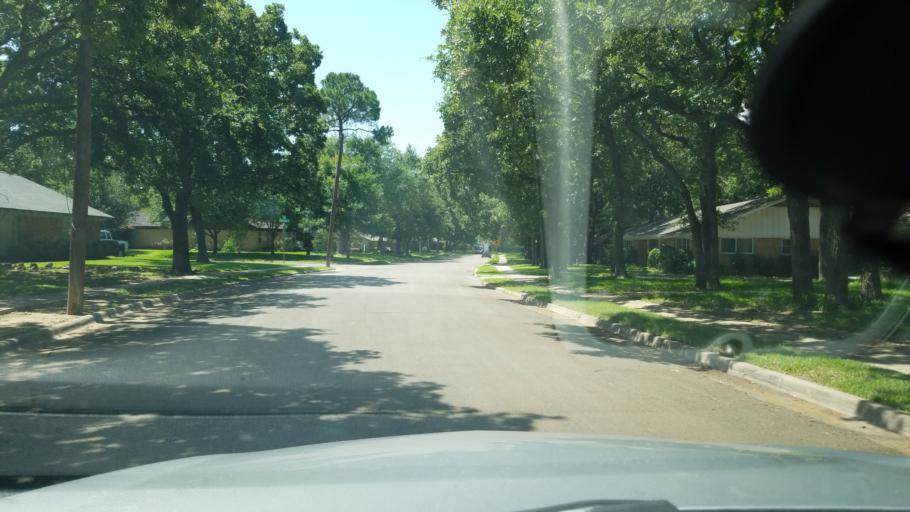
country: US
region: Texas
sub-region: Dallas County
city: Irving
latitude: 32.8335
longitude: -96.9575
